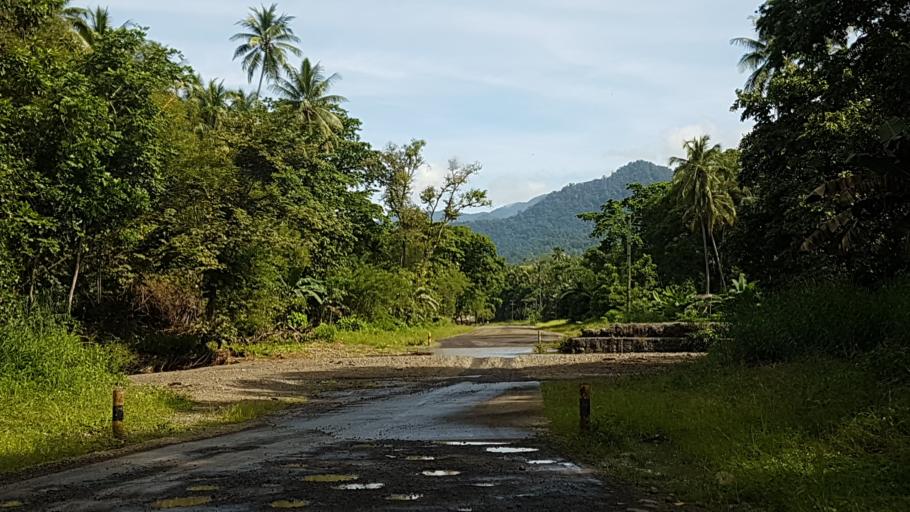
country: PG
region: Milne Bay
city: Alotau
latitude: -10.3248
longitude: 150.4973
